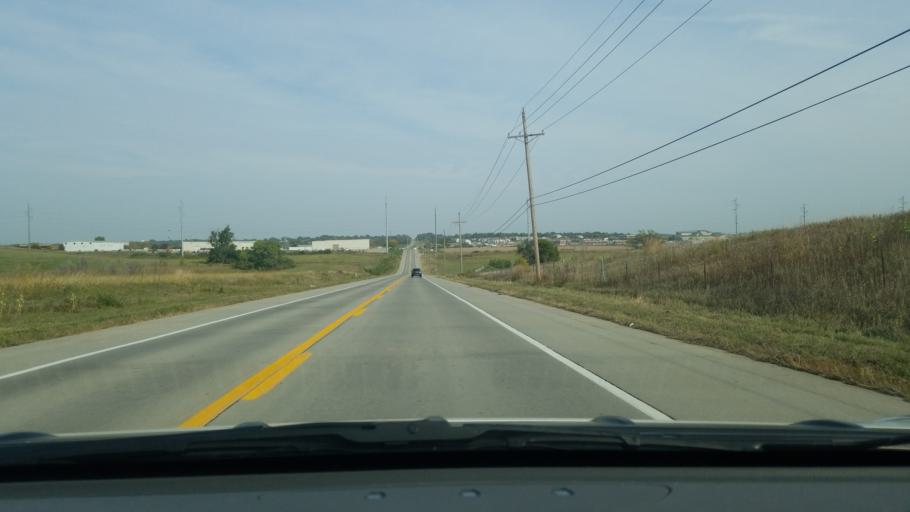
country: US
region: Nebraska
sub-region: Sarpy County
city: Chalco
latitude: 41.1640
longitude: -96.1196
